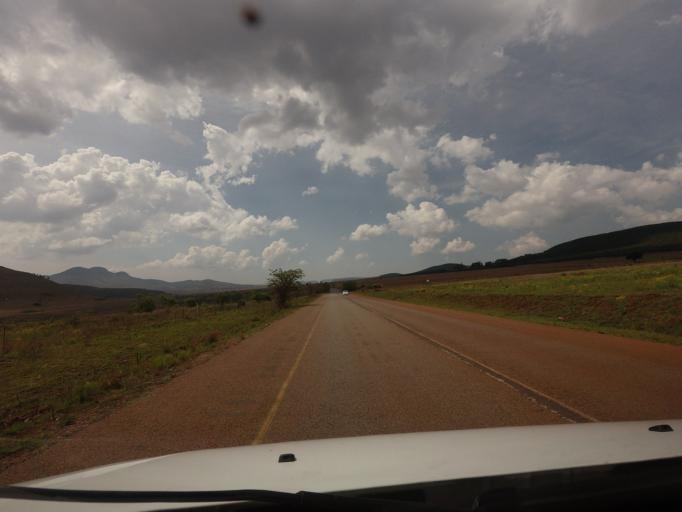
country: ZA
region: Mpumalanga
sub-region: Ehlanzeni District
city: Graksop
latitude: -24.7037
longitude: 30.8192
